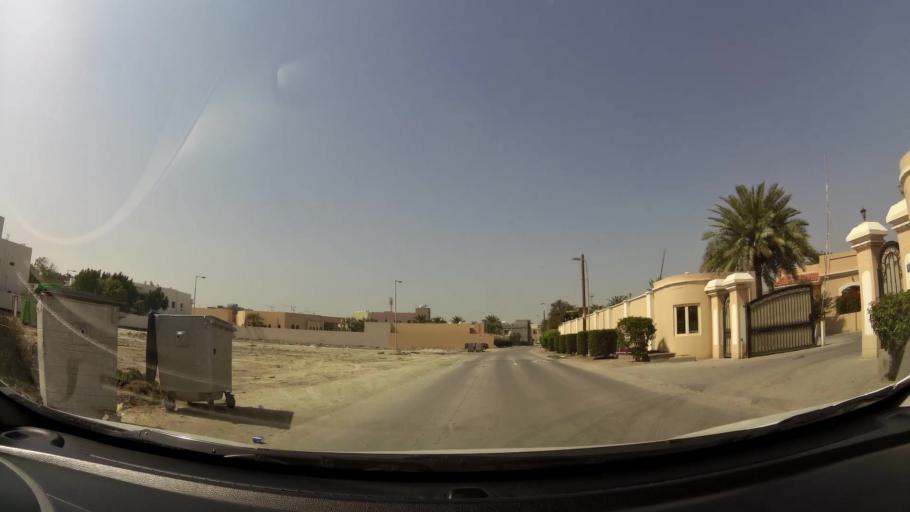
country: BH
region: Northern
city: Madinat `Isa
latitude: 26.1948
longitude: 50.4670
